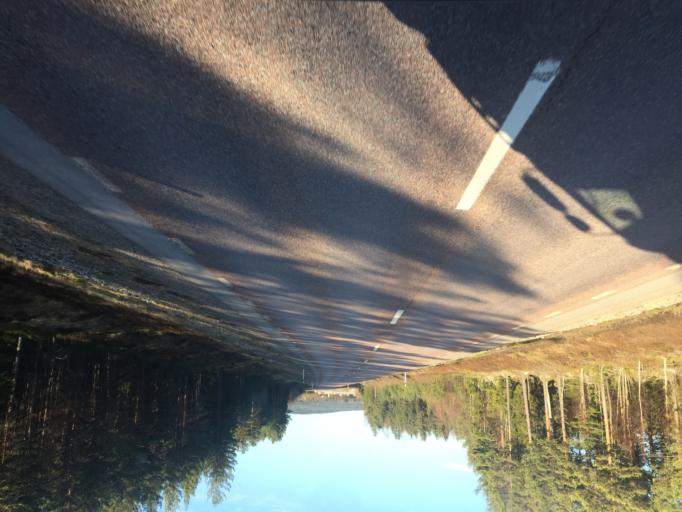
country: SE
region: Dalarna
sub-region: Gagnefs Kommun
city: Mockfjard
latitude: 60.4664
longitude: 14.6936
